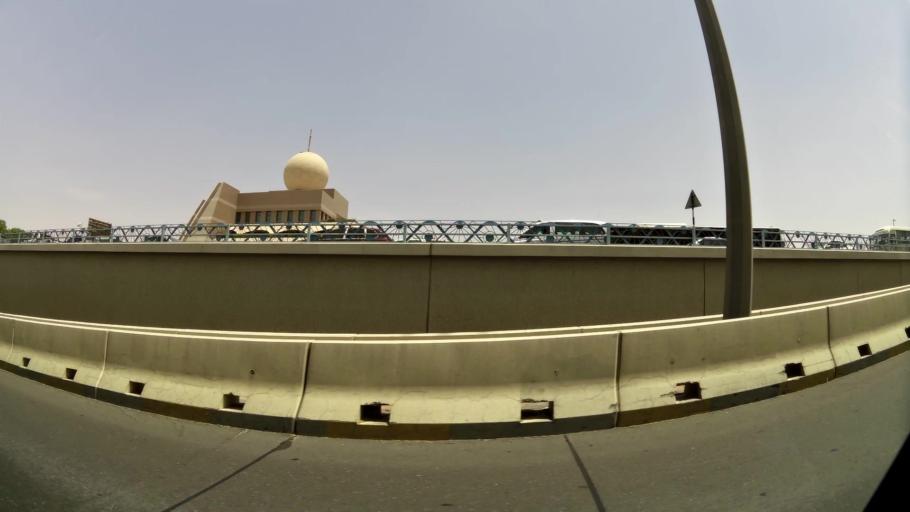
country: AE
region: Abu Dhabi
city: Al Ain
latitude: 24.2057
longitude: 55.7627
